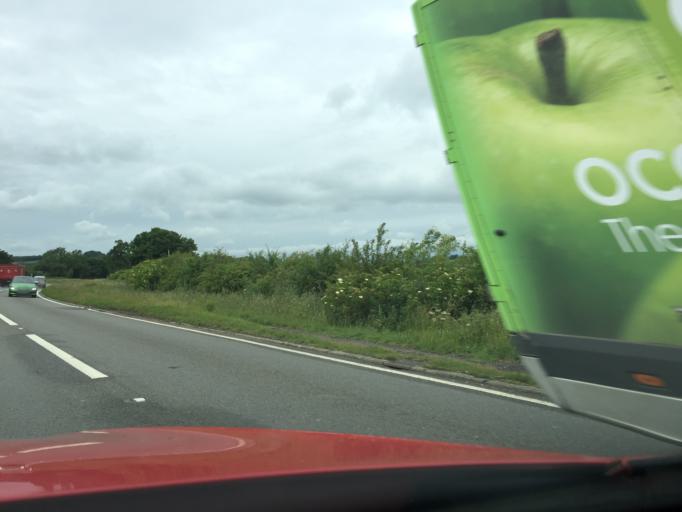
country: GB
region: England
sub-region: Northamptonshire
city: Daventry
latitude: 52.2366
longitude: -1.1134
